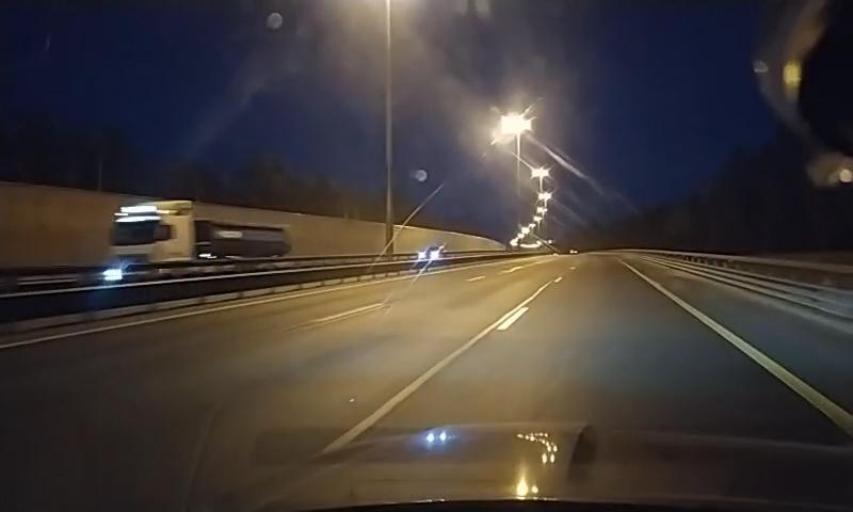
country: RU
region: St.-Petersburg
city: Pesochnyy
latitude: 60.1122
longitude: 30.0815
